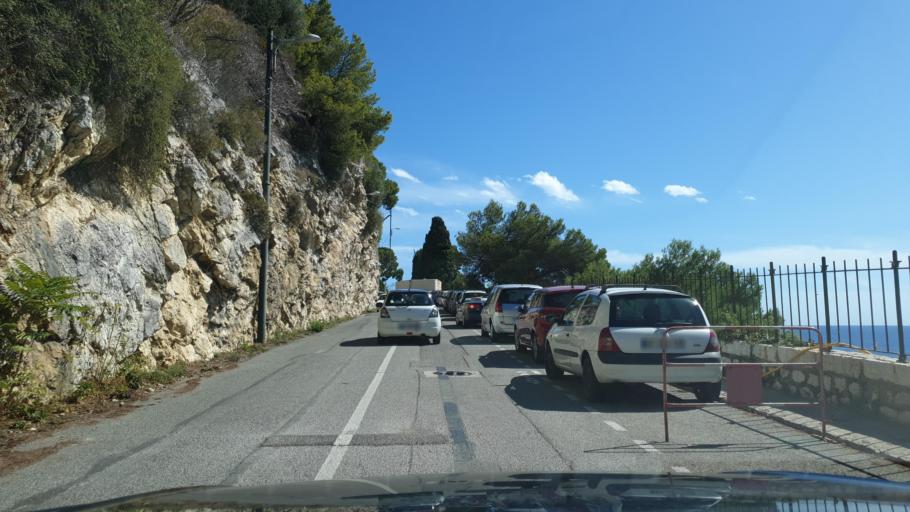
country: FR
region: Provence-Alpes-Cote d'Azur
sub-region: Departement des Alpes-Maritimes
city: Eze
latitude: 43.7192
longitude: 7.3716
